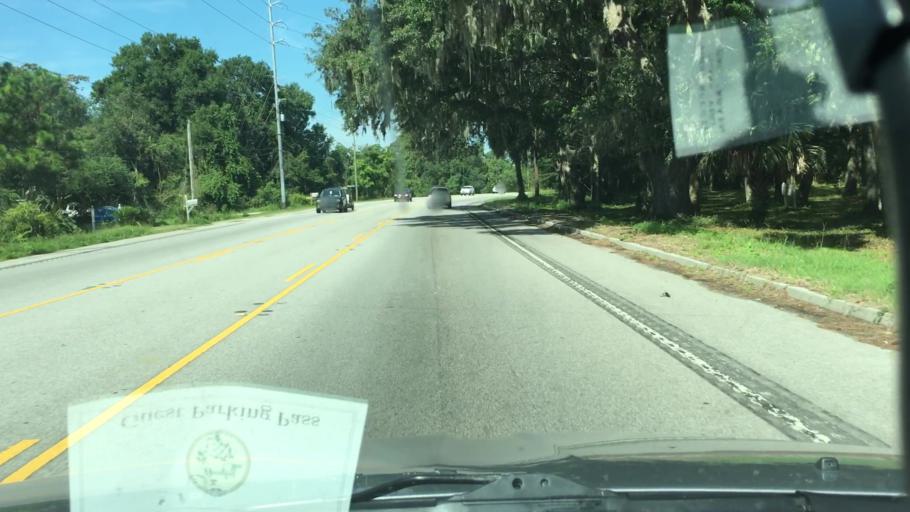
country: US
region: South Carolina
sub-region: Beaufort County
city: Beaufort
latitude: 32.3970
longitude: -80.6040
